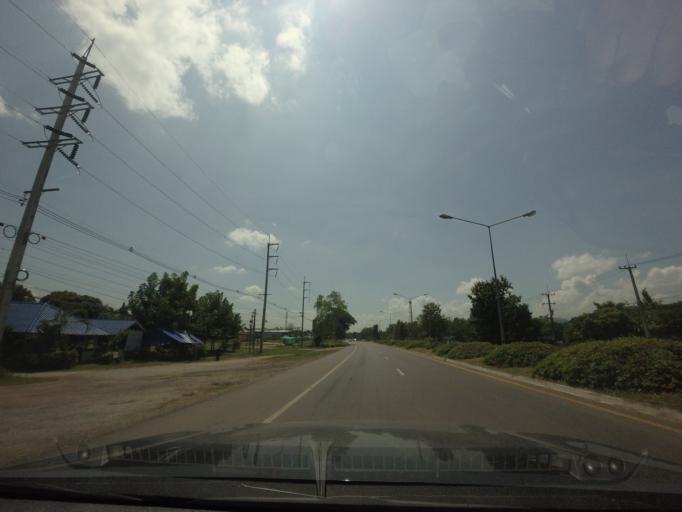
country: TH
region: Phetchabun
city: Lom Sak
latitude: 16.6812
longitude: 101.1626
